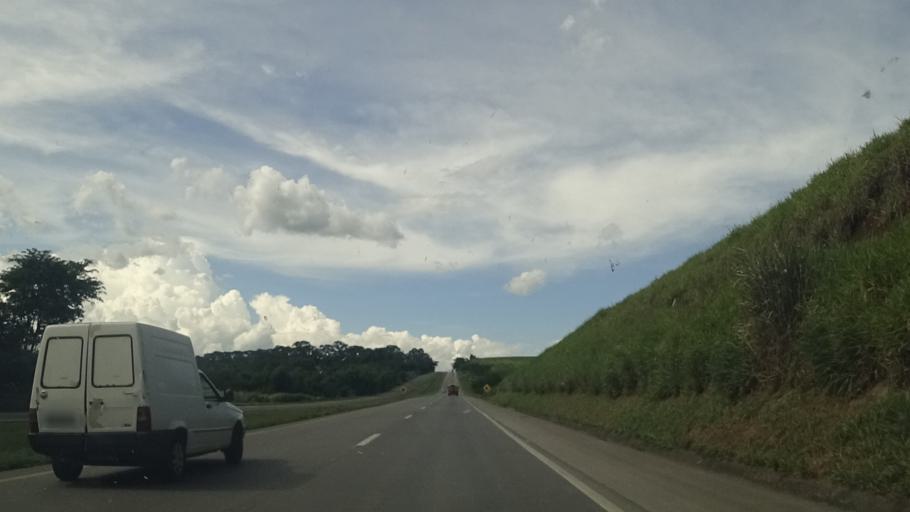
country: BR
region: Goias
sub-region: Piracanjuba
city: Piracanjuba
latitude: -17.1983
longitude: -49.2082
